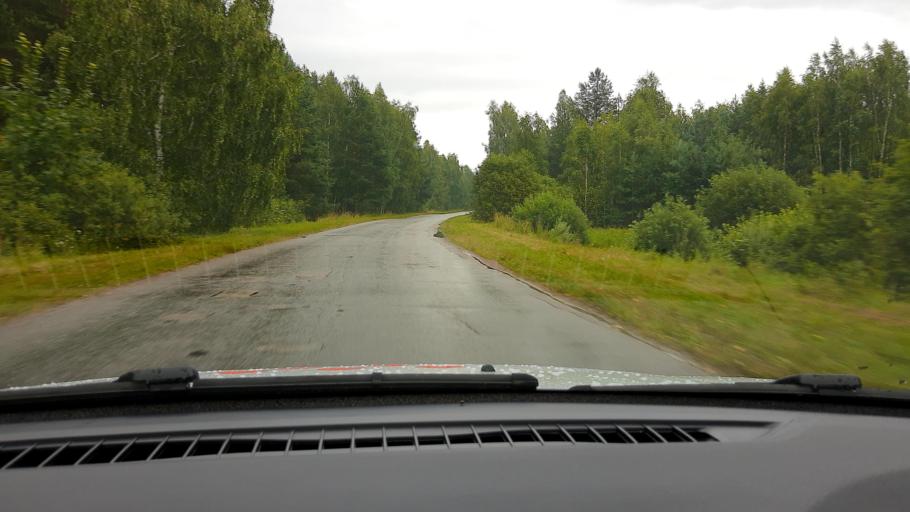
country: RU
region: Nizjnij Novgorod
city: Surovatikha
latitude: 55.9531
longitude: 43.9558
